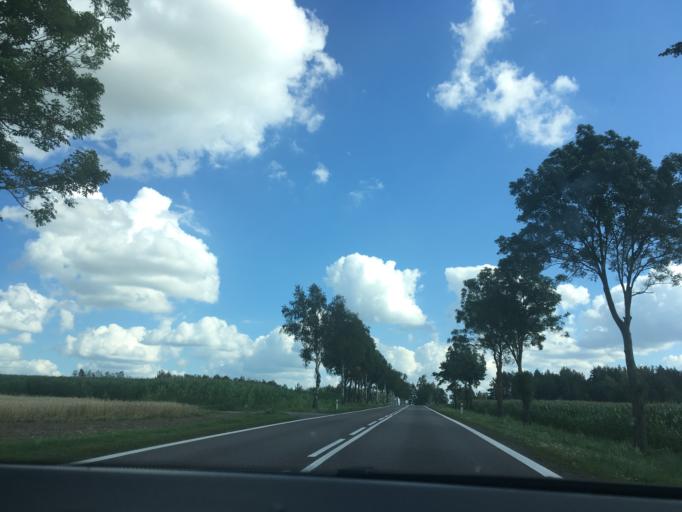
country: PL
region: Podlasie
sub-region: Powiat sokolski
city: Janow
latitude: 53.4149
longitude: 23.1160
